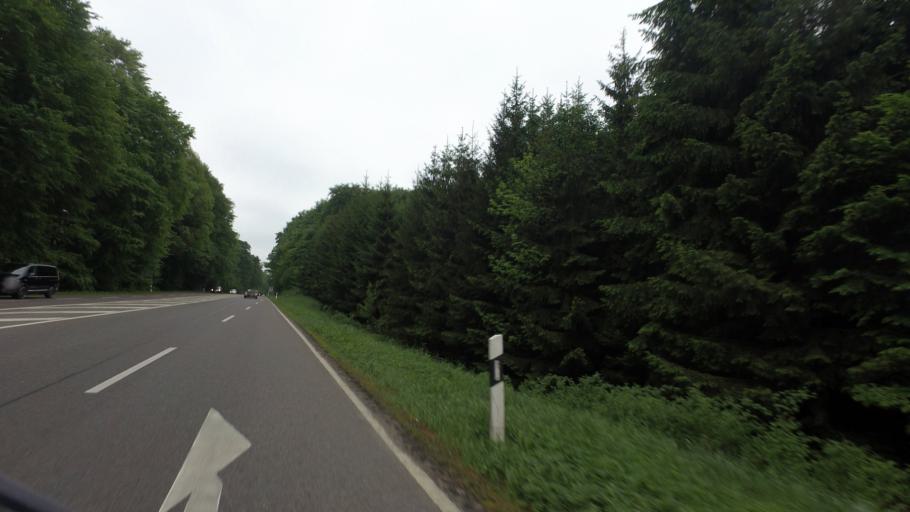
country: DE
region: Mecklenburg-Vorpommern
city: Gross Nemerow
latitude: 53.5113
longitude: 13.2556
